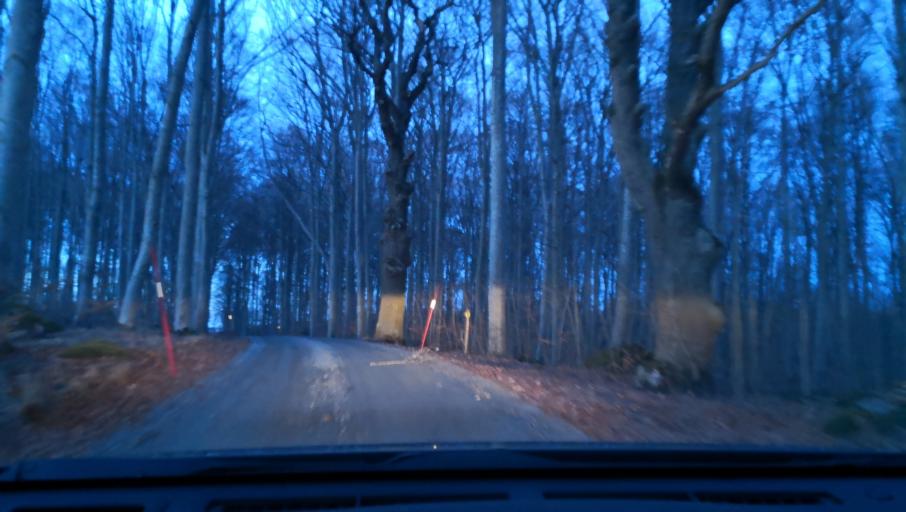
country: SE
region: Uppsala
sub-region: Enkopings Kommun
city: Dalby
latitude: 59.5695
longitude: 17.3779
